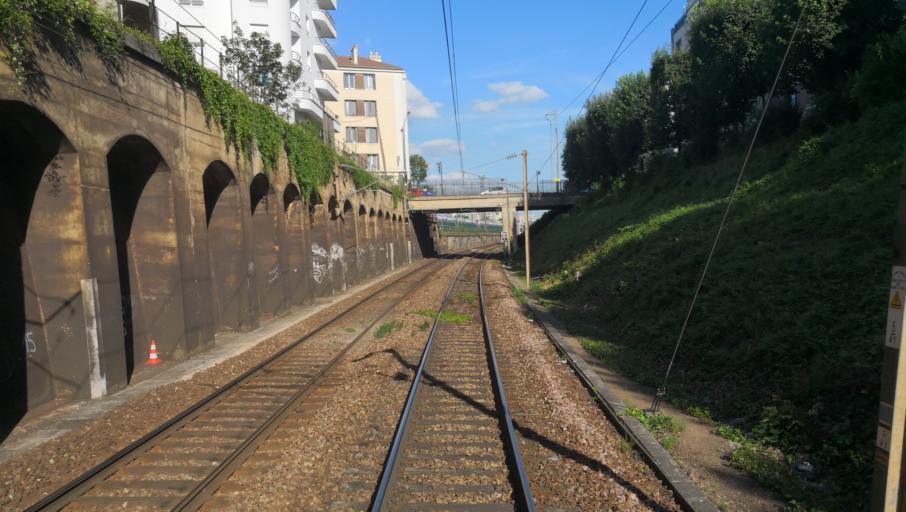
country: FR
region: Ile-de-France
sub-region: Departement des Hauts-de-Seine
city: Bois-Colombes
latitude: 48.9122
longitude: 2.2715
